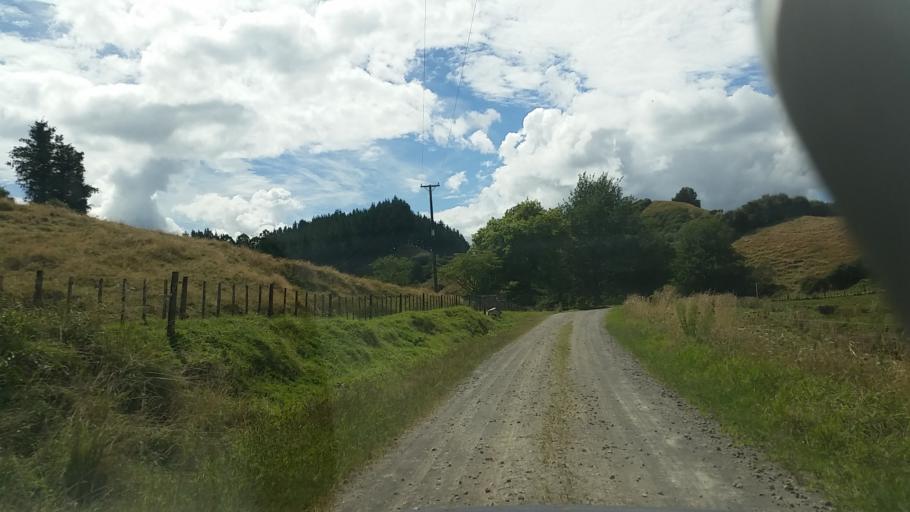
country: NZ
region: Taranaki
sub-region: South Taranaki District
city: Eltham
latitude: -39.2591
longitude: 174.5657
